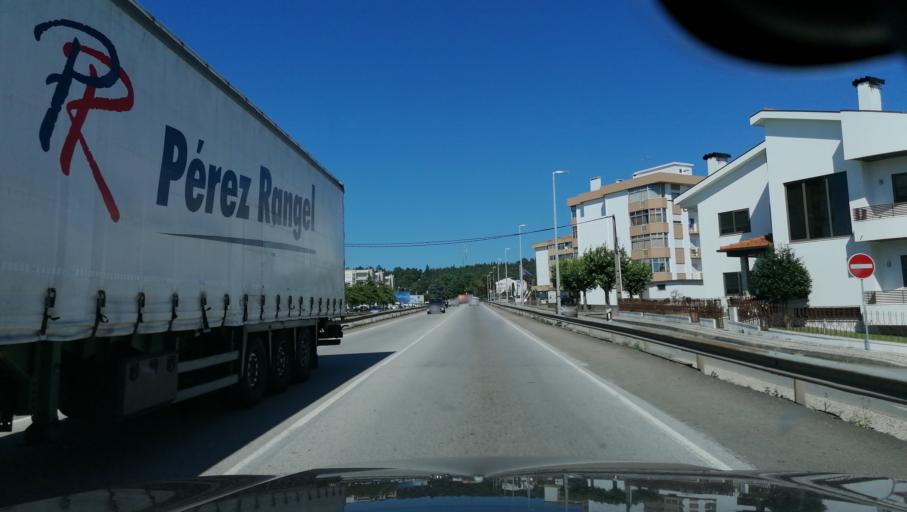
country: PT
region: Aveiro
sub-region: Santa Maria da Feira
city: Feira
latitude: 40.9270
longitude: -8.5579
